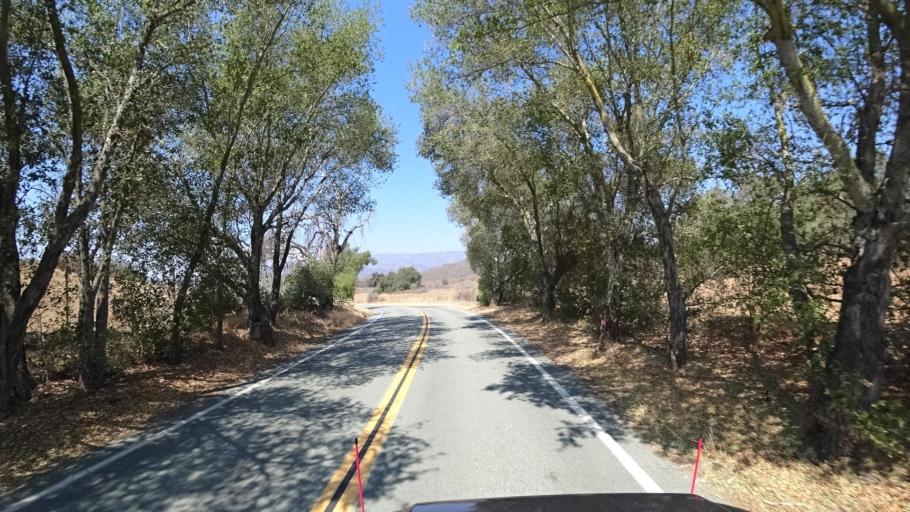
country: US
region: California
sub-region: San Diego County
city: Fallbrook
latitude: 33.4096
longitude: -117.2925
